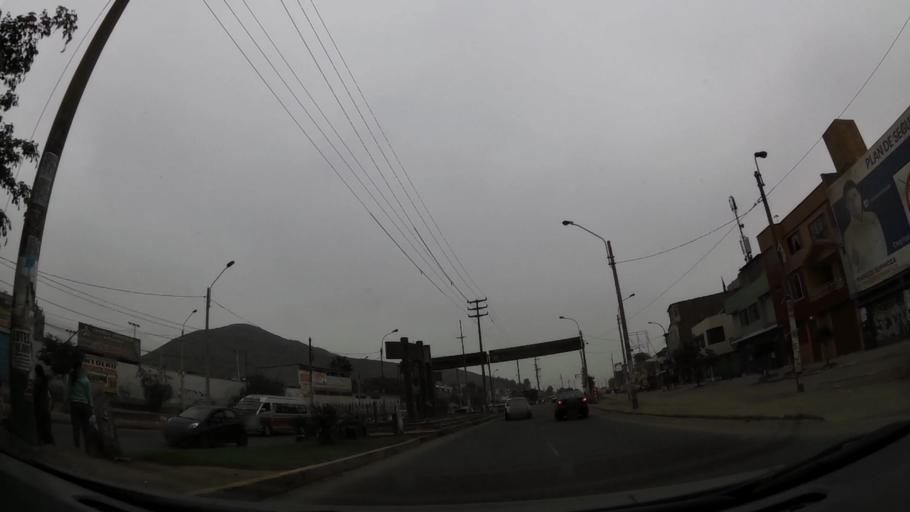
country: PE
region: Lima
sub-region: Lima
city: Urb. Santo Domingo
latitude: -11.9078
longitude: -77.0329
